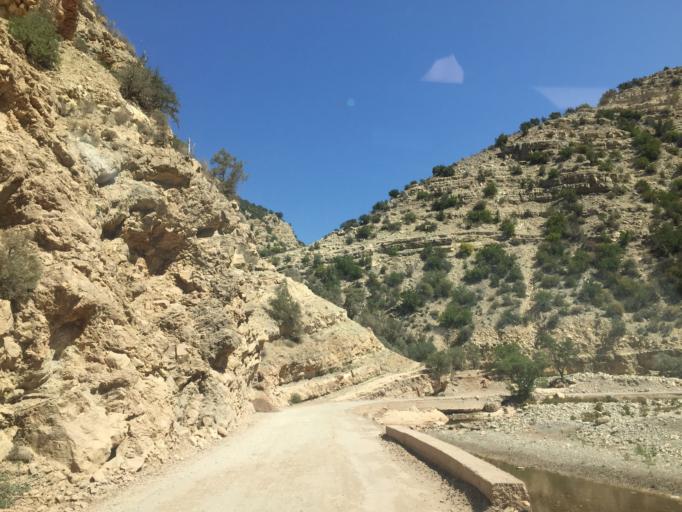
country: MA
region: Souss-Massa-Draa
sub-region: Agadir-Ida-ou-Tnan
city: Aourir
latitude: 30.5635
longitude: -9.5426
